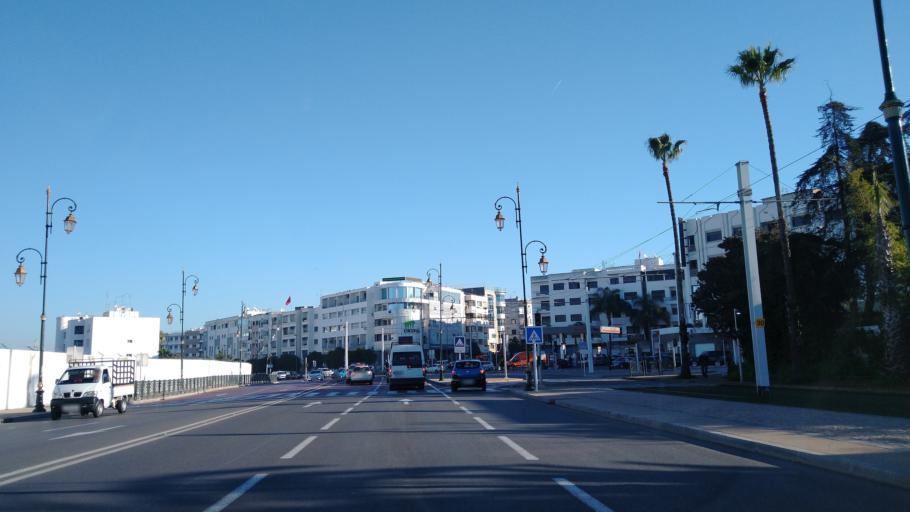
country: MA
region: Rabat-Sale-Zemmour-Zaer
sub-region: Rabat
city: Rabat
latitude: 33.9957
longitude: -6.8520
